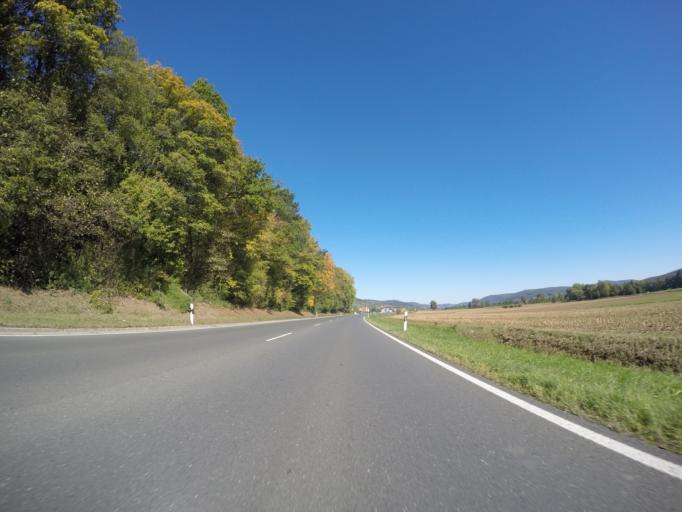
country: DE
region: Bavaria
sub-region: Upper Franconia
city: Kirchehrenbach
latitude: 49.7364
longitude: 11.1309
